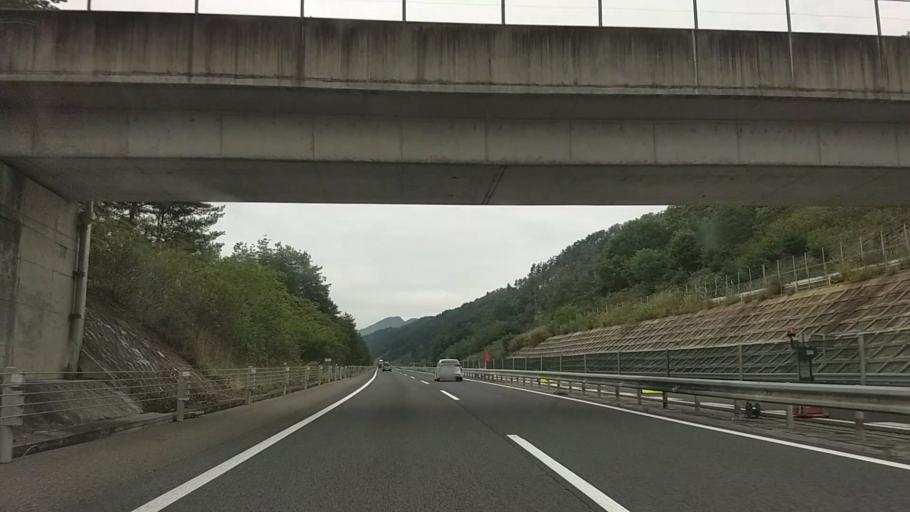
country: JP
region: Nagano
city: Hotaka
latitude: 36.4123
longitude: 138.0017
